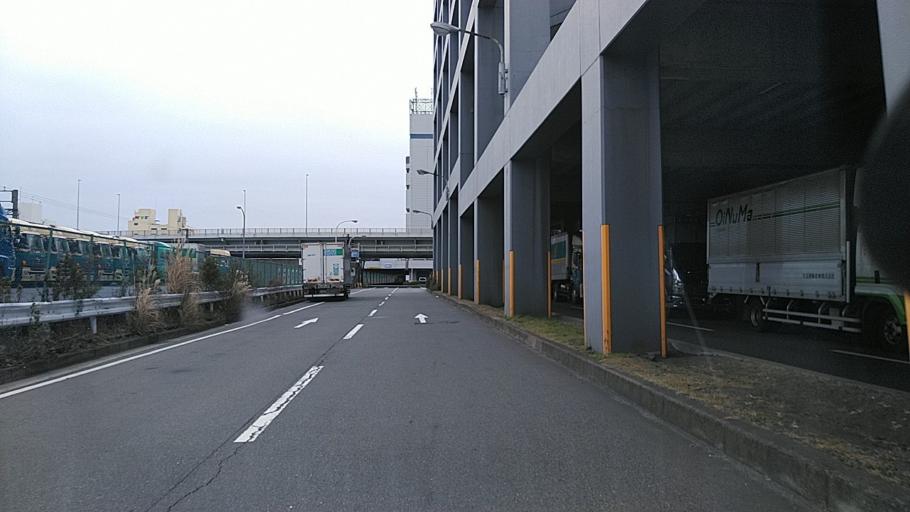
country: JP
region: Kanagawa
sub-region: Kawasaki-shi
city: Kawasaki
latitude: 35.5962
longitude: 139.7613
